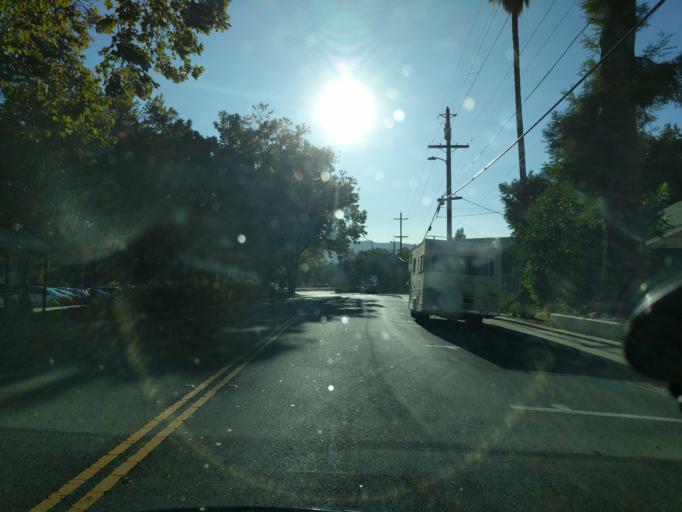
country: US
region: California
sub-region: Alameda County
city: Pleasanton
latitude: 37.6586
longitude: -121.8792
